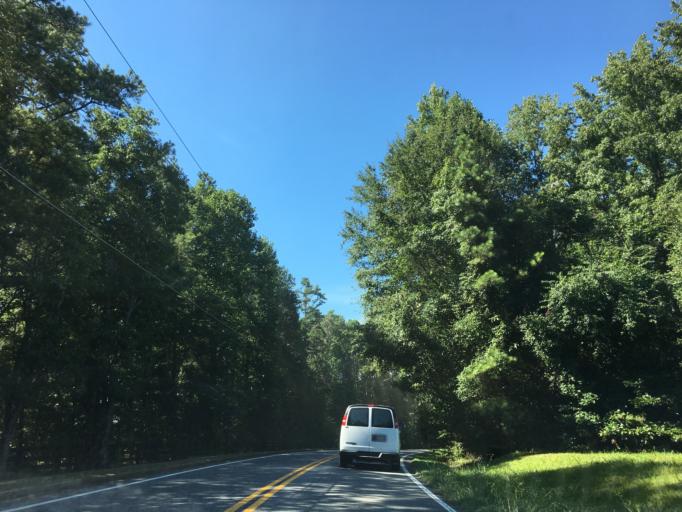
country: US
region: Georgia
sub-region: Fulton County
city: Milton
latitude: 34.1476
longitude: -84.2857
